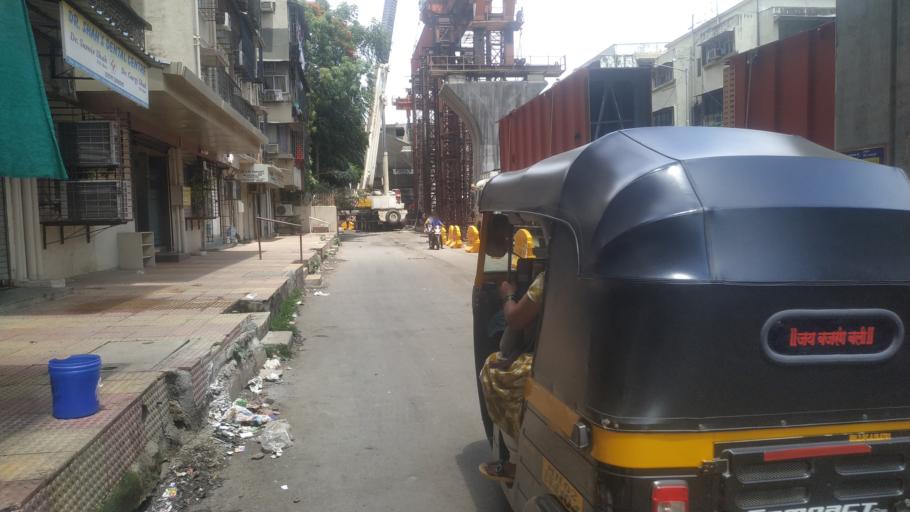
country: IN
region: Maharashtra
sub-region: Mumbai Suburban
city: Mumbai
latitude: 19.0519
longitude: 72.8681
